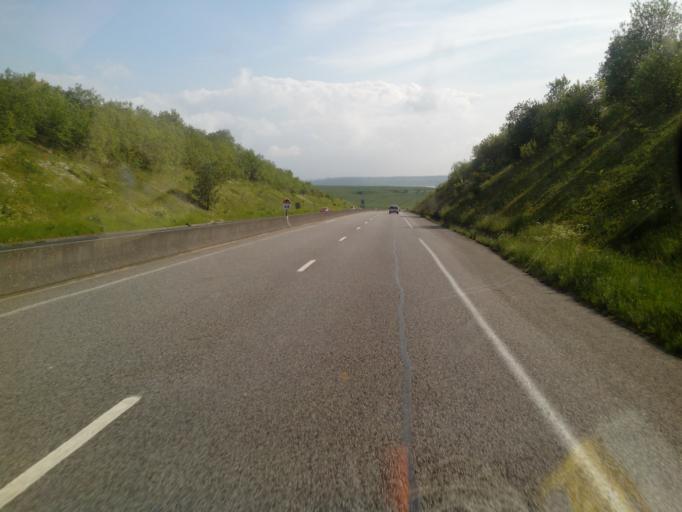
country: FR
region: Haute-Normandie
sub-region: Departement de la Seine-Maritime
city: Foucarmont
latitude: 49.7981
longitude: 1.5049
